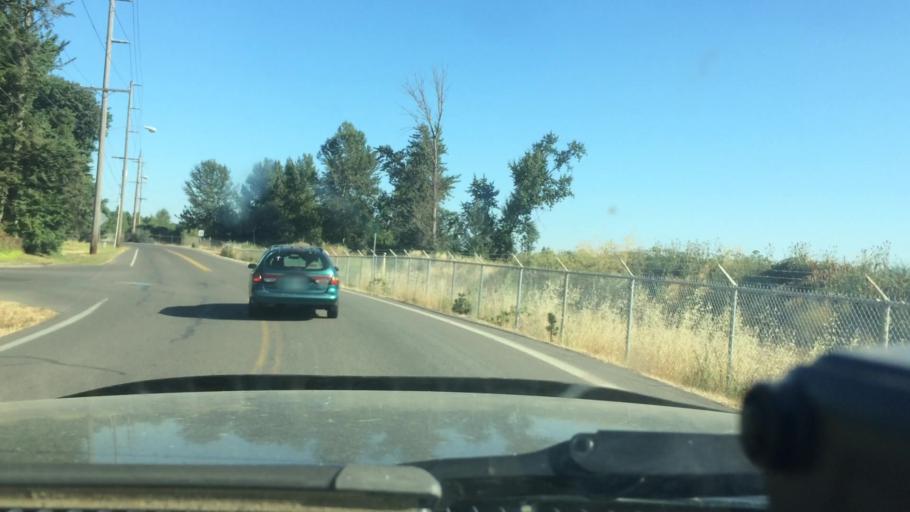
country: US
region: Oregon
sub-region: Lane County
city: Eugene
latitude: 44.1009
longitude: -123.1143
